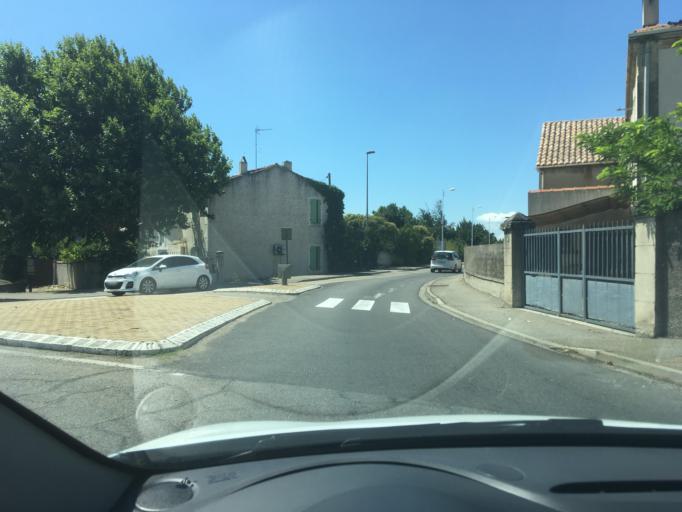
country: FR
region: Provence-Alpes-Cote d'Azur
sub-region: Departement des Bouches-du-Rhone
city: Chateaurenard
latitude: 43.8880
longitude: 4.8444
